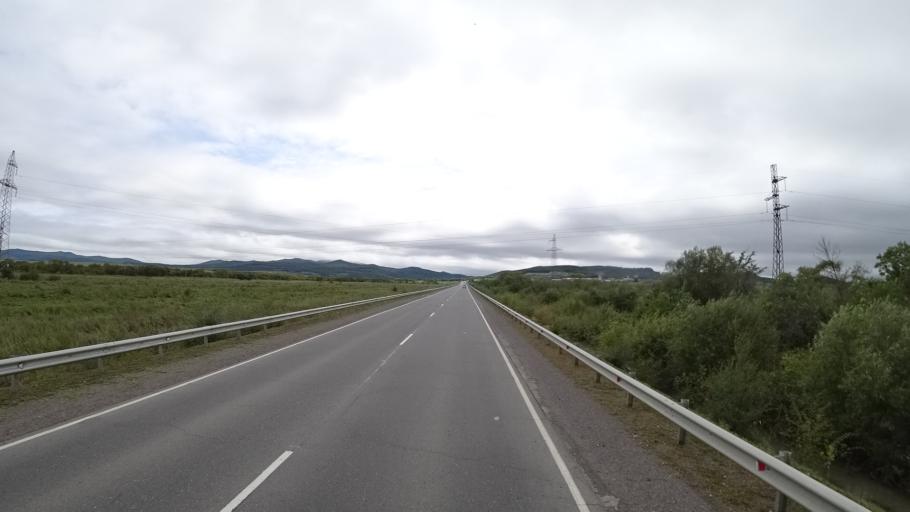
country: RU
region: Primorskiy
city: Monastyrishche
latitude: 44.1815
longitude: 132.4416
